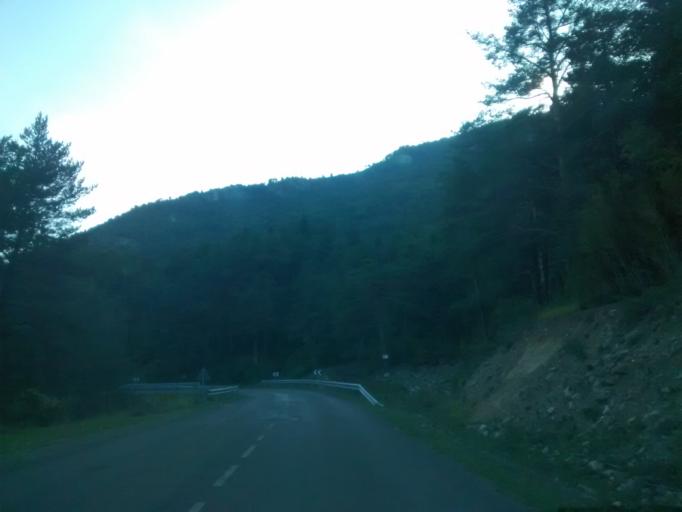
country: ES
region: Aragon
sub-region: Provincia de Huesca
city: Anso
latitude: 42.7943
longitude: -0.7357
